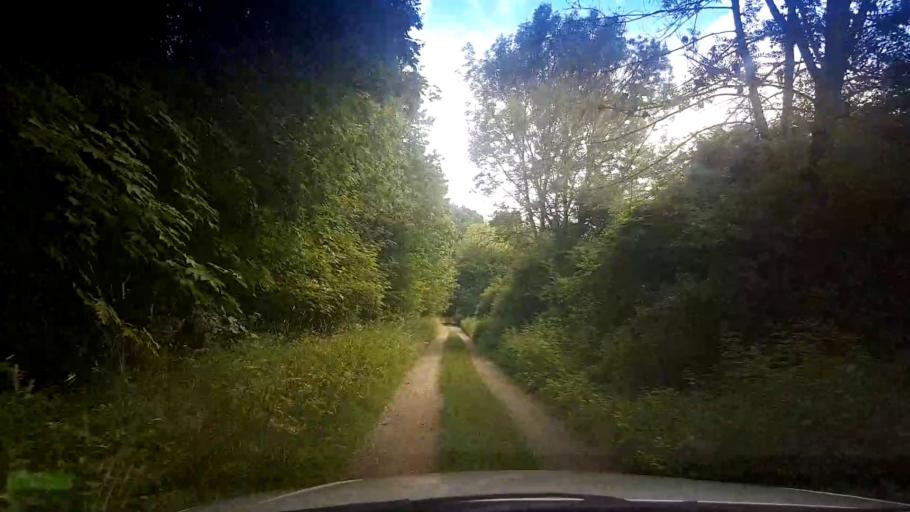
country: DE
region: Bavaria
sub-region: Upper Franconia
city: Memmelsdorf
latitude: 49.9525
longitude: 10.9869
